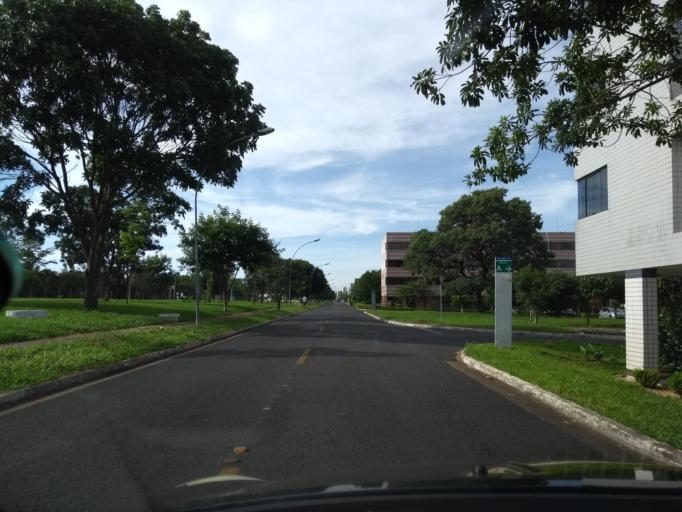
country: BR
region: Federal District
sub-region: Brasilia
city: Brasilia
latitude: -15.7869
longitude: -47.9289
